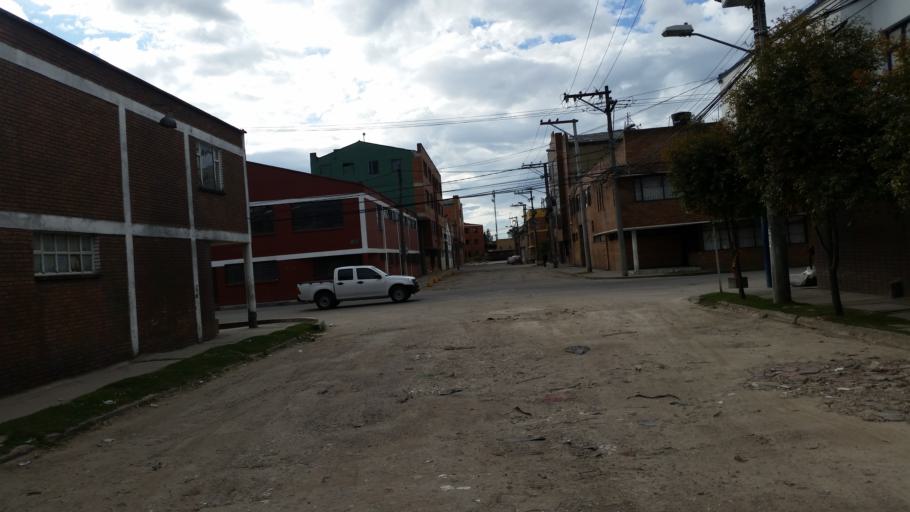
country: CO
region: Bogota D.C.
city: Bogota
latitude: 4.6294
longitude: -74.0990
